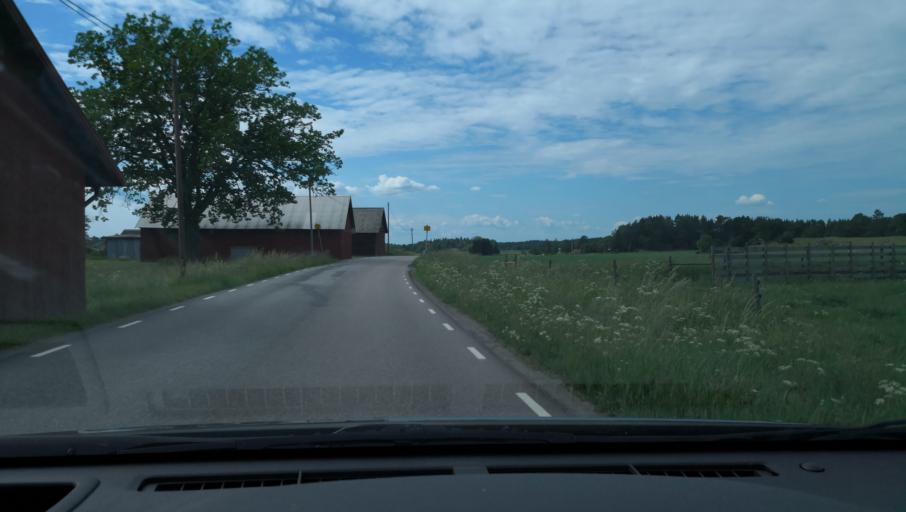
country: SE
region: Uppsala
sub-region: Uppsala Kommun
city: Uppsala
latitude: 59.8127
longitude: 17.5079
